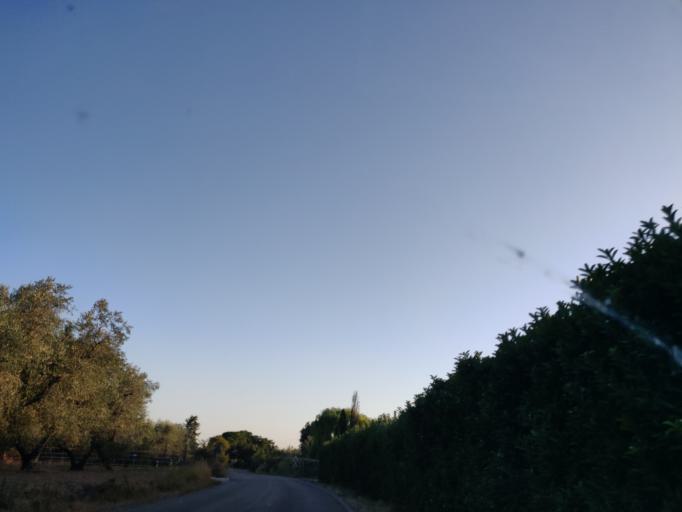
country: IT
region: Latium
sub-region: Provincia di Viterbo
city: Canino
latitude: 42.4175
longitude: 11.7044
